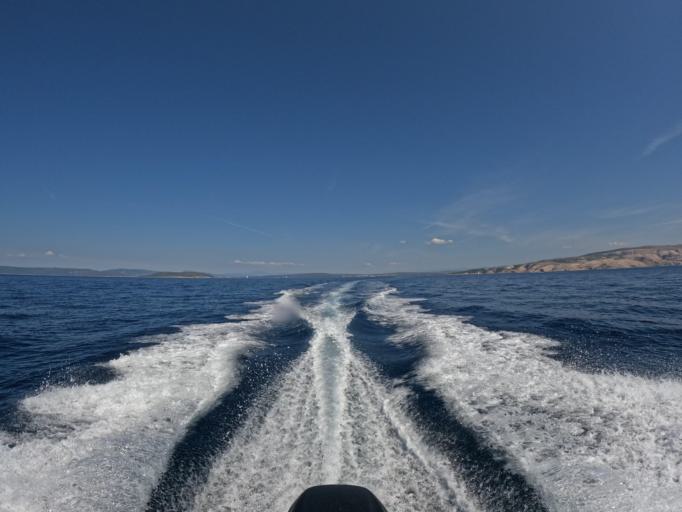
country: HR
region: Primorsko-Goranska
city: Punat
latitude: 44.9211
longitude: 14.6214
